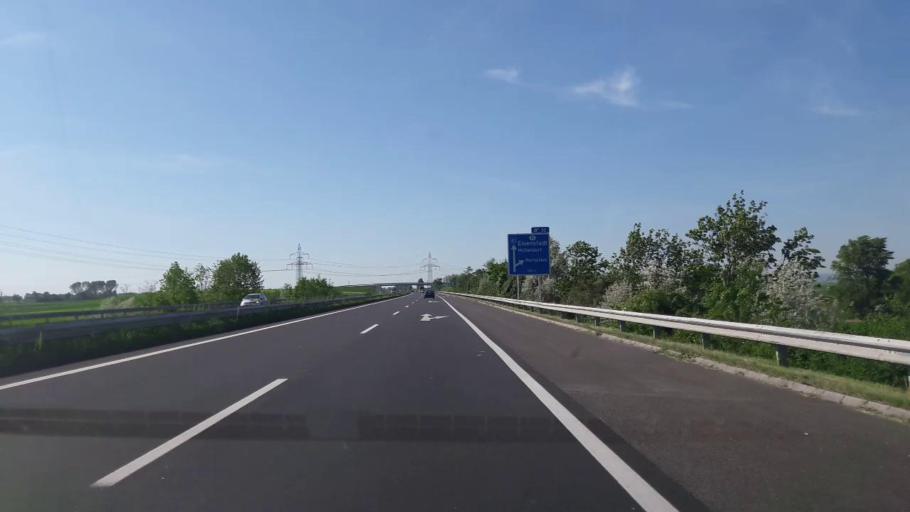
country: AT
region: Burgenland
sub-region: Eisenstadt-Umgebung
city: Hornstein
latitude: 47.8827
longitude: 16.4152
